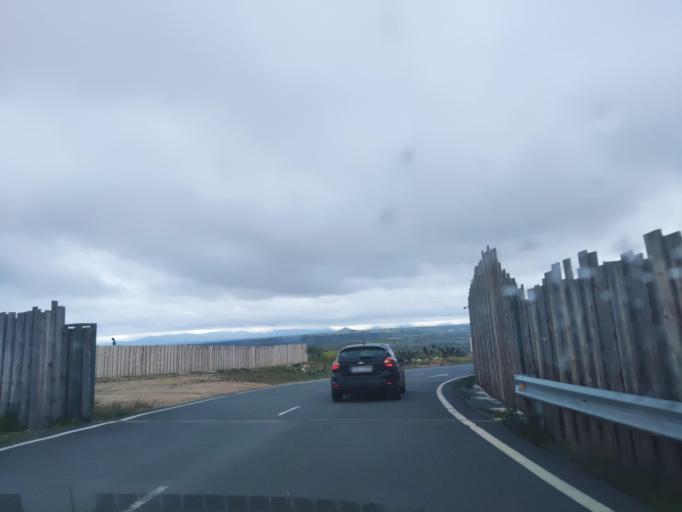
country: ES
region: Castille-La Mancha
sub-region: Province of Toledo
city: Toledo
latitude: 39.8411
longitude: -4.0873
